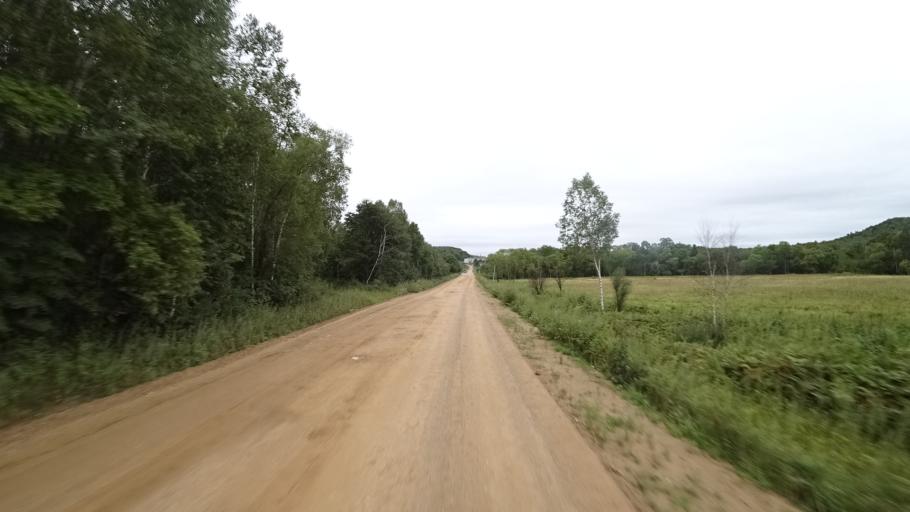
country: RU
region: Primorskiy
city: Rettikhovka
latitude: 44.1791
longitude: 132.8753
